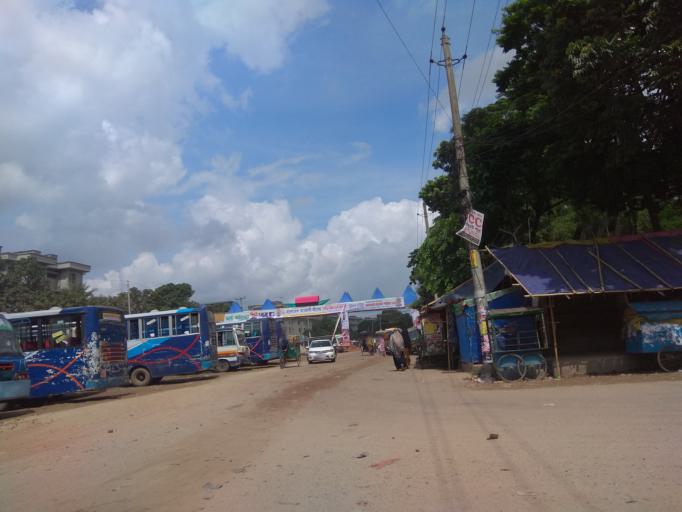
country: BD
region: Dhaka
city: Paltan
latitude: 23.7984
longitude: 90.3885
